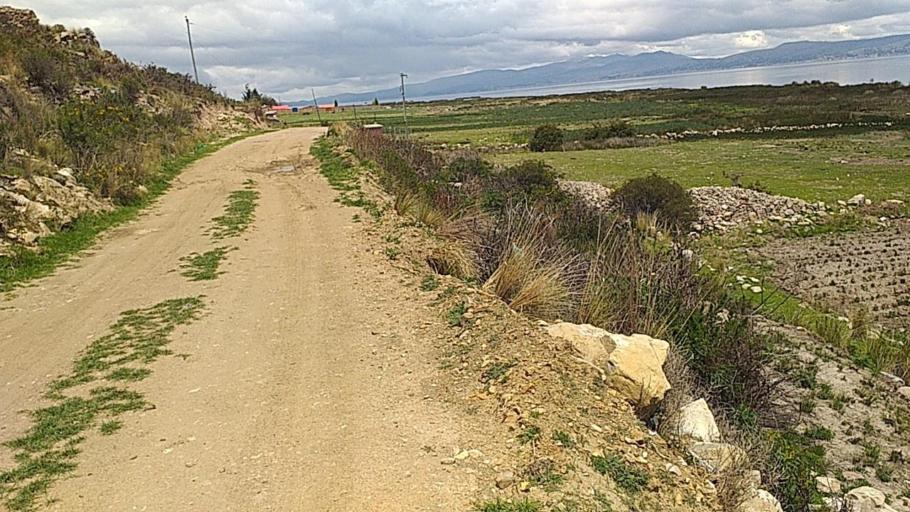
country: BO
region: La Paz
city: Huatajata
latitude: -16.3154
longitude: -68.6732
